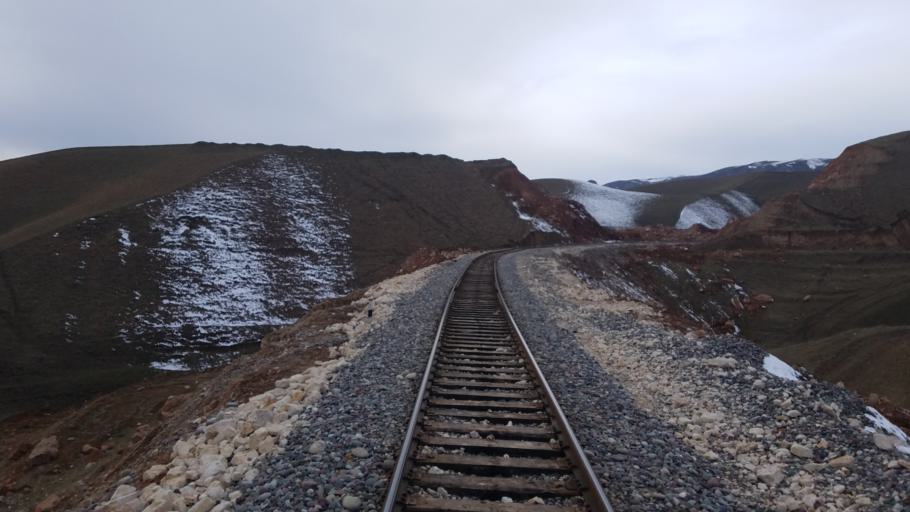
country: TJ
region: Khatlon
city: Yovon
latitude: 38.3709
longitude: 68.9395
